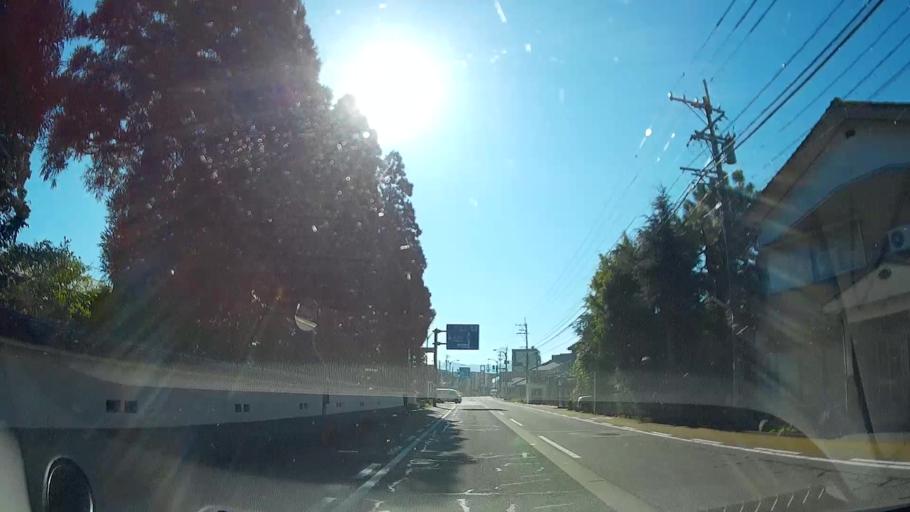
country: JP
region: Toyama
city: Nanto-shi
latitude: 36.6339
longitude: 136.9466
